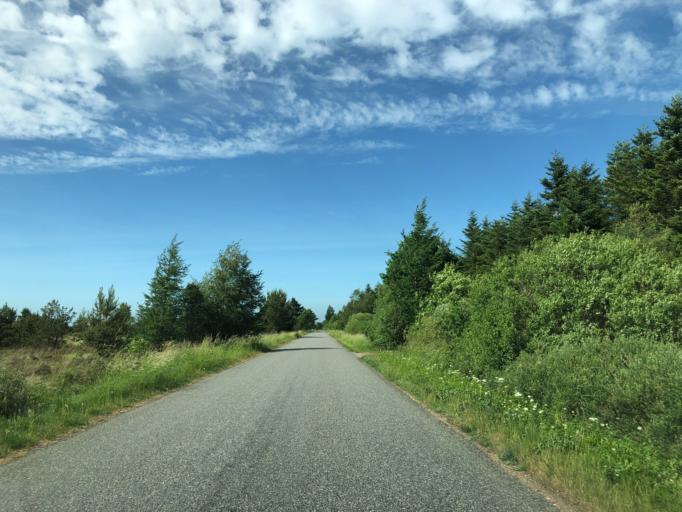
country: DK
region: Central Jutland
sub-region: Herning Kommune
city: Snejbjerg
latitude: 56.0707
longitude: 8.9152
